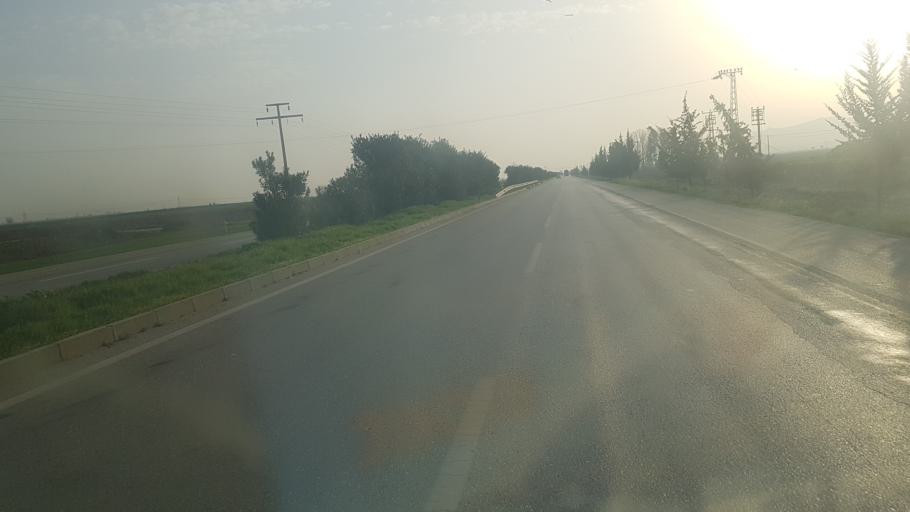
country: TR
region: Adana
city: Ceyhan
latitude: 37.0575
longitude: 35.8893
